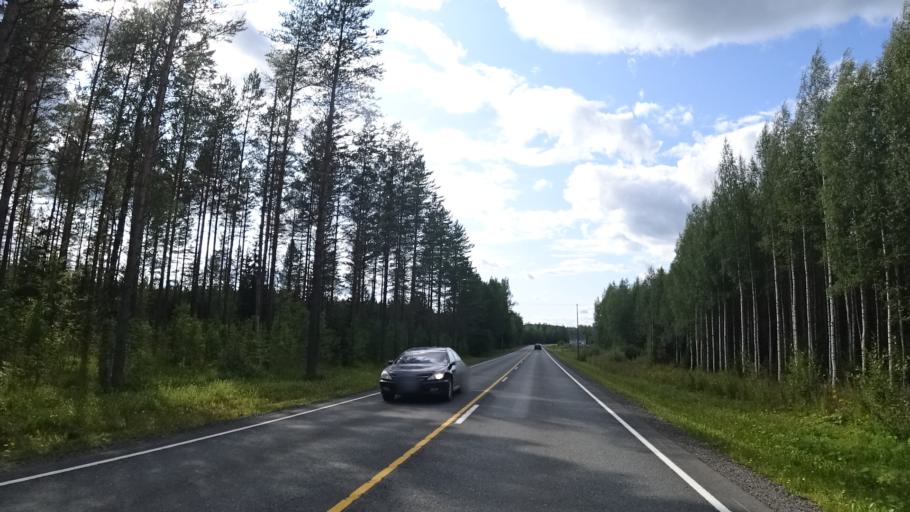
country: FI
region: North Karelia
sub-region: Keski-Karjala
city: Tohmajaervi
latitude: 62.1844
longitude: 30.4795
